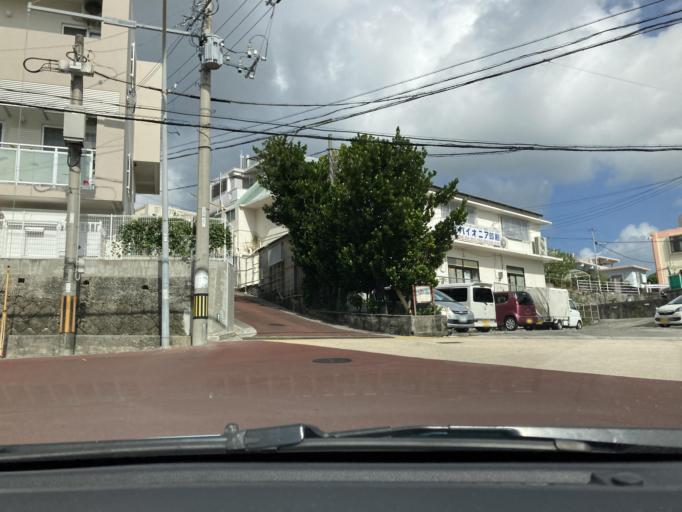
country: JP
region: Okinawa
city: Naha-shi
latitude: 26.2022
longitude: 127.7082
